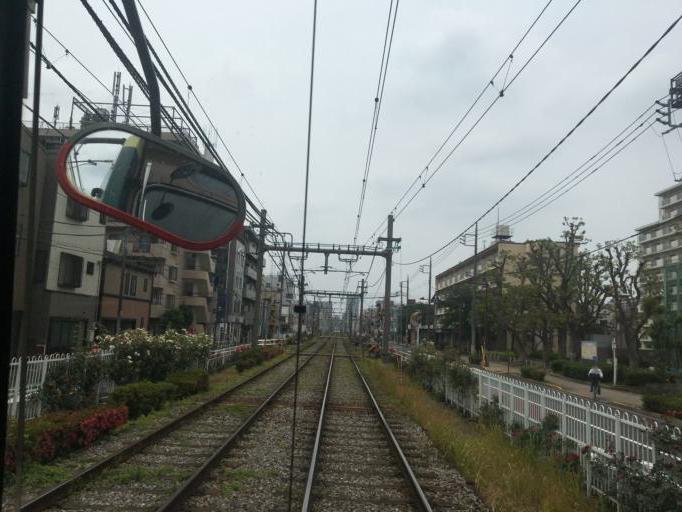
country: JP
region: Saitama
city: Kawaguchi
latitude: 35.7507
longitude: 139.7573
